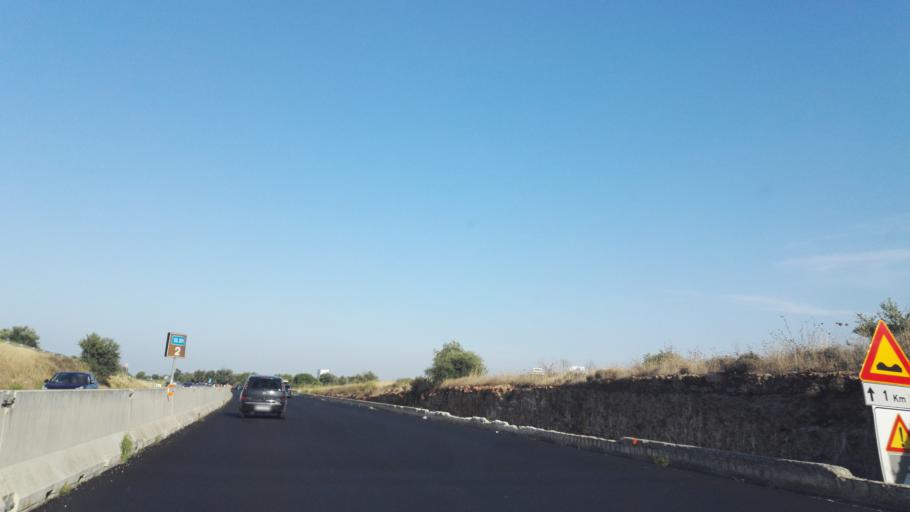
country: IT
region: Apulia
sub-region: Provincia di Brindisi
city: Fasano
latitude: 40.8349
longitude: 17.3904
